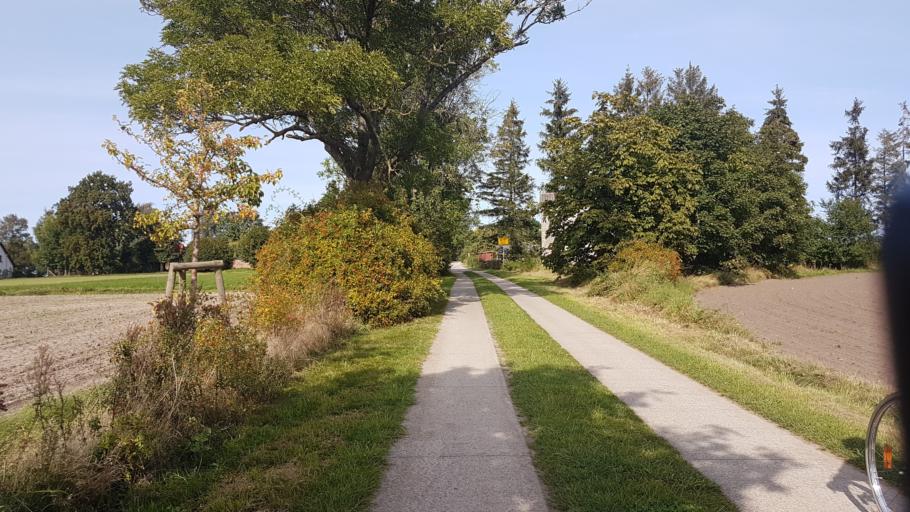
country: DE
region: Mecklenburg-Vorpommern
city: Gingst
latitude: 54.4184
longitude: 13.2556
